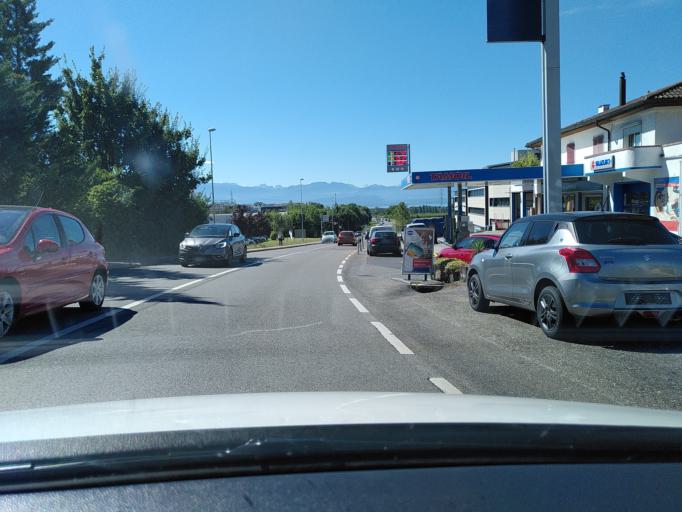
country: CH
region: Vaud
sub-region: Morges District
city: Aubonne
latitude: 46.4901
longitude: 6.3990
